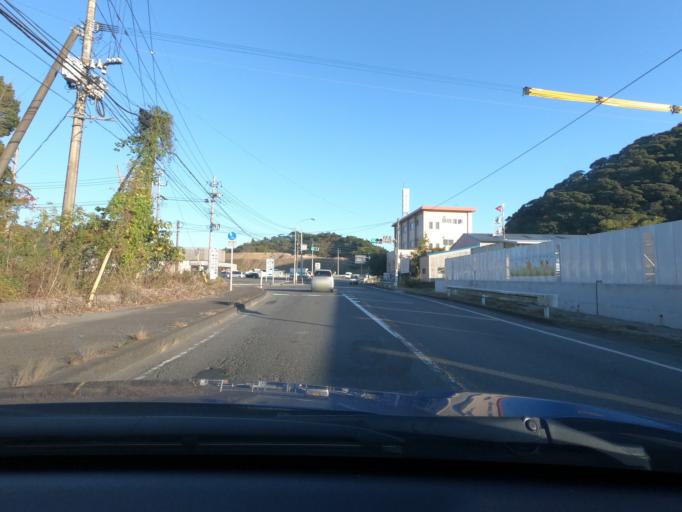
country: JP
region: Kagoshima
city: Satsumasendai
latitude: 31.8469
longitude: 130.2708
